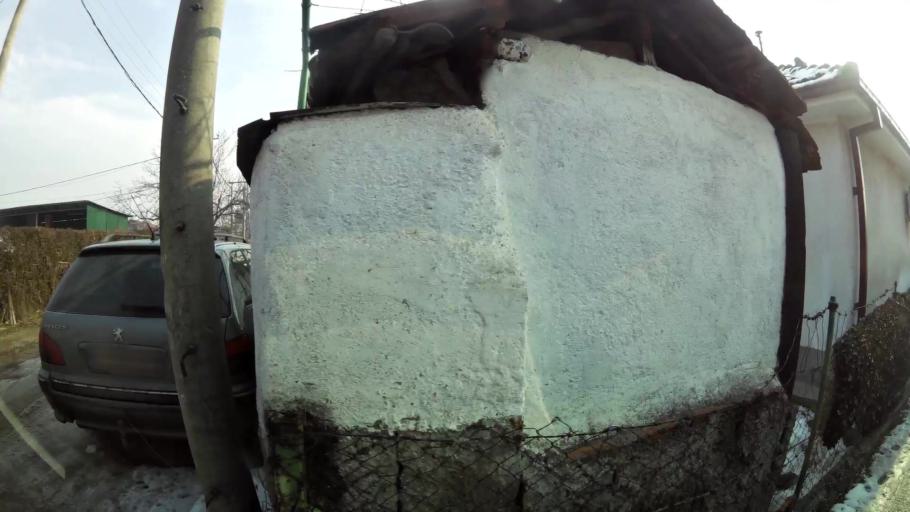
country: MK
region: Kisela Voda
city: Kisela Voda
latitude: 41.9921
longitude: 21.4980
